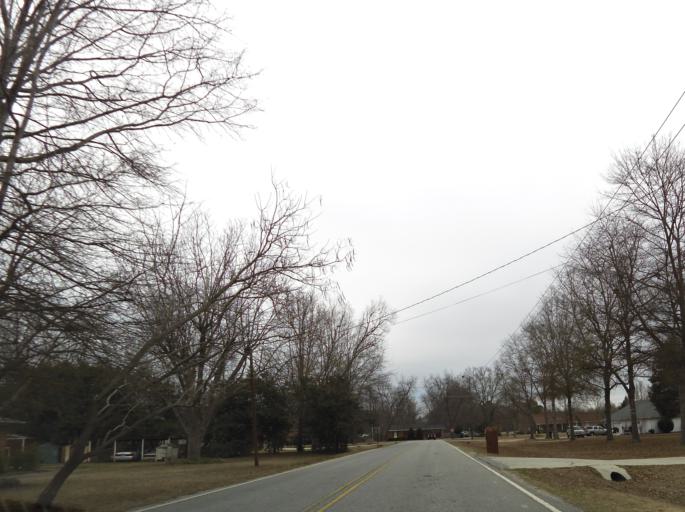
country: US
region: Georgia
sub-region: Houston County
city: Centerville
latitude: 32.7030
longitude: -83.6845
